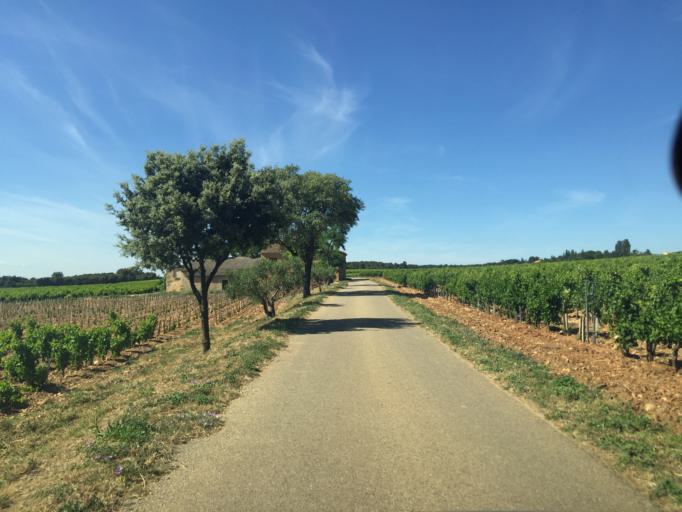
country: FR
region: Provence-Alpes-Cote d'Azur
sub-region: Departement du Vaucluse
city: Chateauneuf-du-Pape
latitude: 44.0726
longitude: 4.8063
